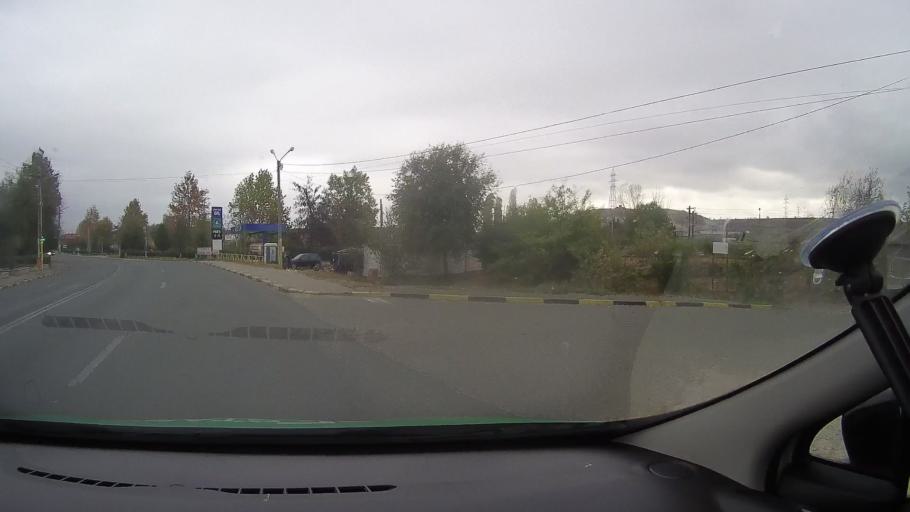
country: RO
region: Constanta
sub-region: Oras Murfatlar
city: Murfatlar
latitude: 44.1730
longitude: 28.4130
